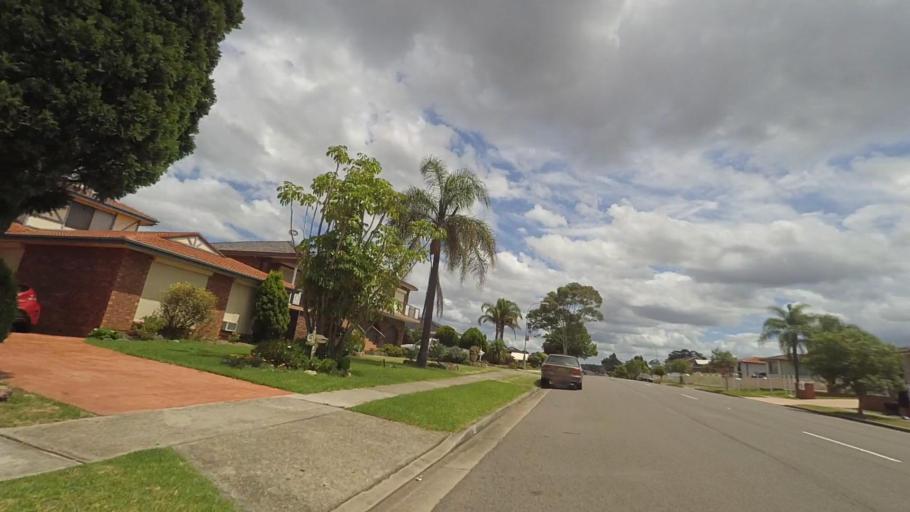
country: AU
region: New South Wales
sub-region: Fairfield
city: Cabramatta West
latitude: -33.8752
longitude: 150.9074
